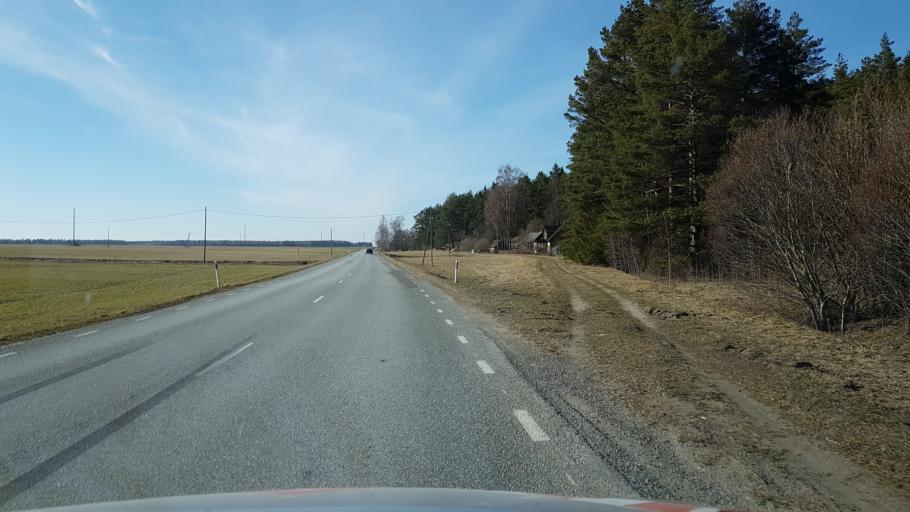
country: EE
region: Laeaene-Virumaa
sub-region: Vinni vald
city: Vinni
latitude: 59.1922
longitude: 26.5698
